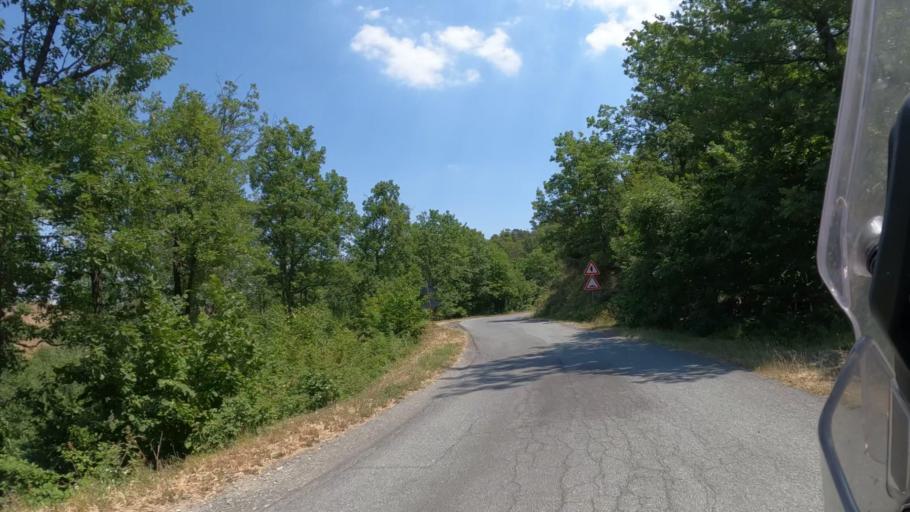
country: IT
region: Piedmont
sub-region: Provincia di Alessandria
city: Morbello
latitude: 44.5571
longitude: 8.5092
